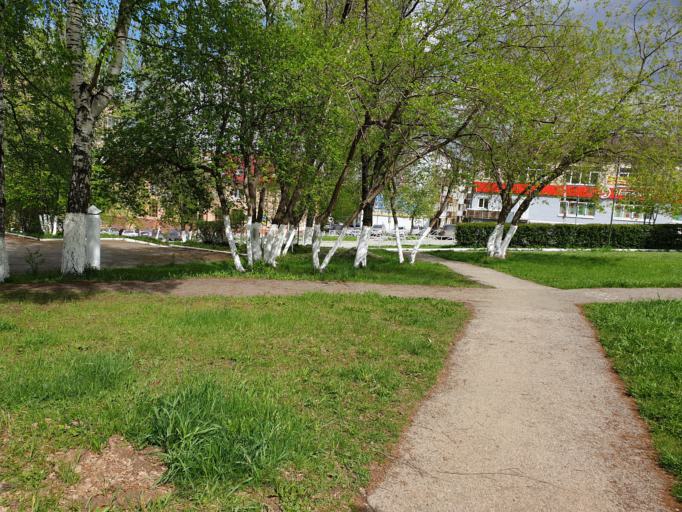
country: RU
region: Sverdlovsk
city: Pervoural'sk
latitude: 56.9089
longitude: 59.9439
